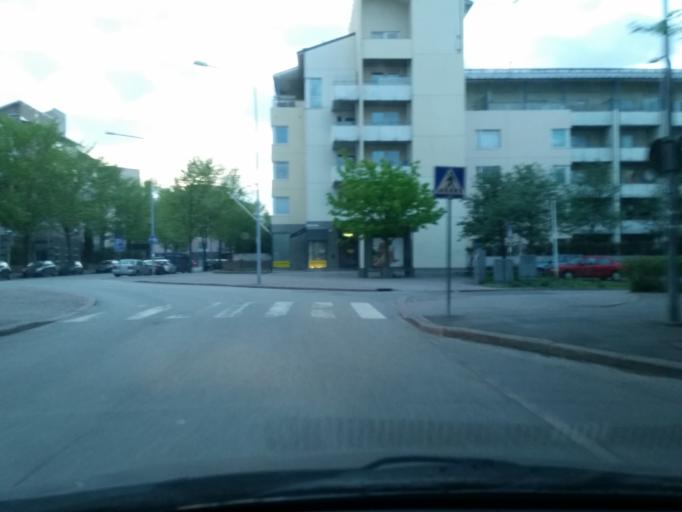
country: FI
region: Uusimaa
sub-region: Helsinki
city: Helsinki
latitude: 60.1892
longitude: 25.0371
